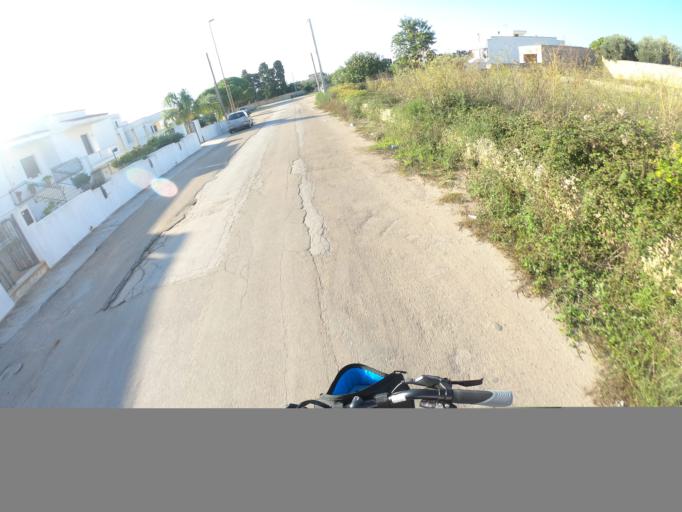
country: IT
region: Apulia
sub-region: Provincia di Lecce
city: Castrignano del Capo
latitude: 39.8360
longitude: 18.3556
